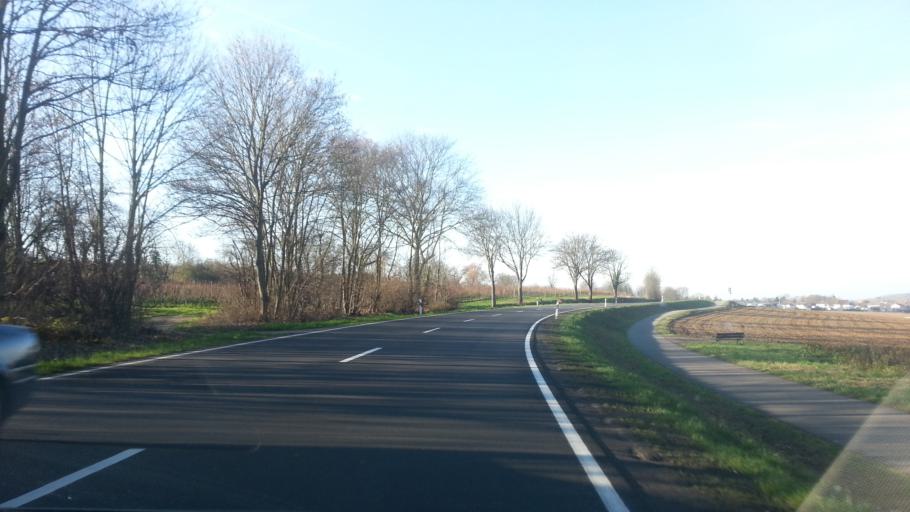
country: DE
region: Rheinland-Pfalz
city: Molsheim
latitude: 49.6339
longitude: 8.1827
